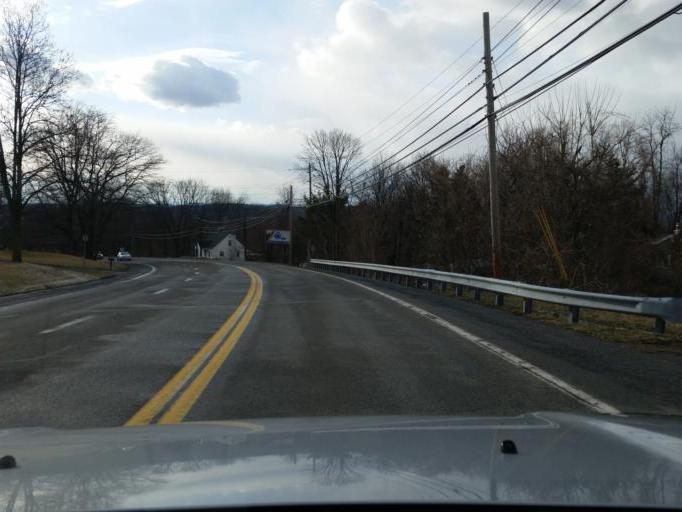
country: US
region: Pennsylvania
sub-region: Dauphin County
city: Middletown
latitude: 40.1970
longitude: -76.6960
